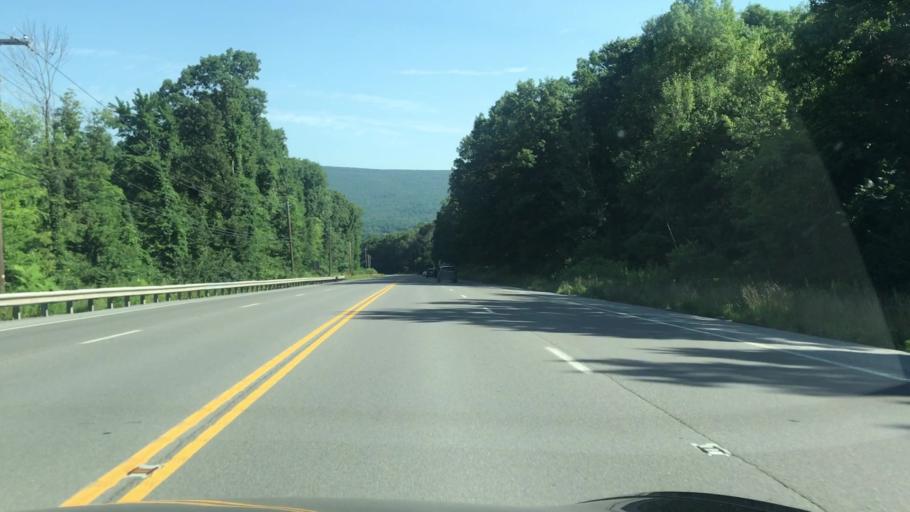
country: US
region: Pennsylvania
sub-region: Lycoming County
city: Montgomery
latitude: 41.1607
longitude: -76.9073
